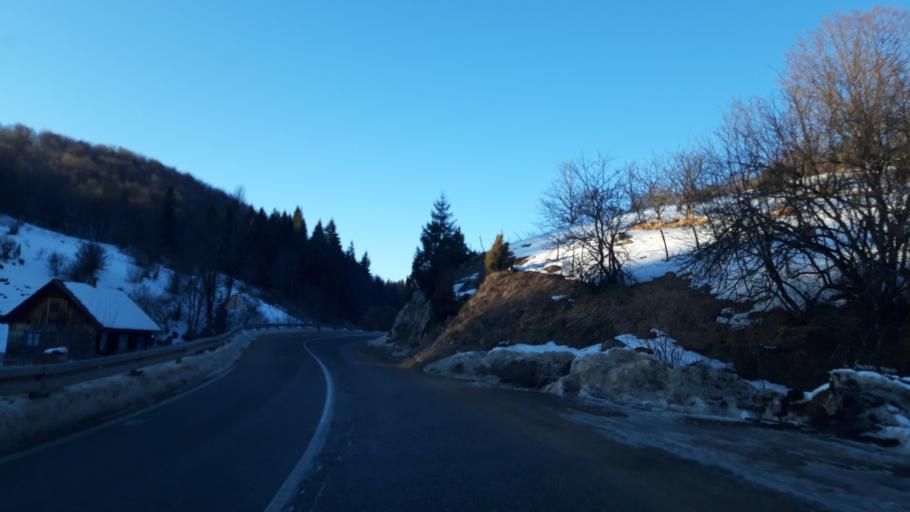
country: BA
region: Republika Srpska
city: Han Pijesak
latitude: 44.1266
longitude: 18.9624
